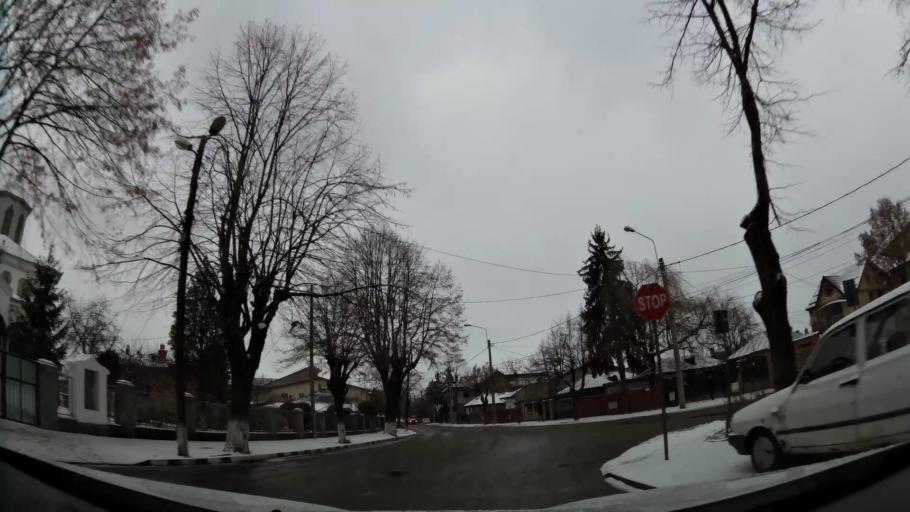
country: RO
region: Prahova
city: Ploiesti
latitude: 44.9357
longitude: 26.0440
